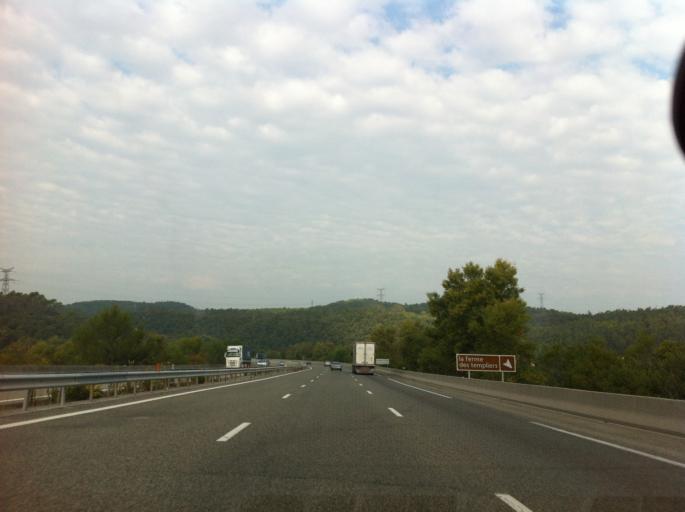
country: FR
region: Provence-Alpes-Cote d'Azur
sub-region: Departement du Var
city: Camps-la-Source
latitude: 43.4177
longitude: 6.1241
